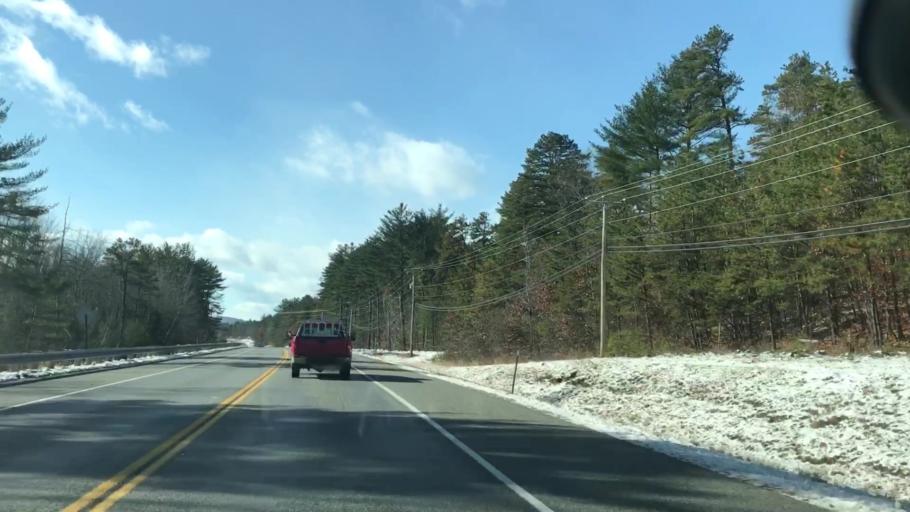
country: US
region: New Hampshire
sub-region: Carroll County
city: Freedom
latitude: 43.7876
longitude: -71.0900
